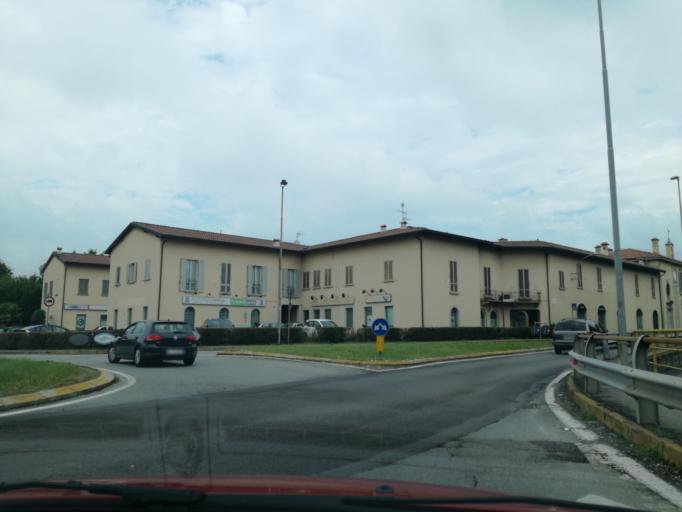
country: IT
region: Lombardy
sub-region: Provincia di Lecco
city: Cernusco Lombardone
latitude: 45.6984
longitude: 9.4068
